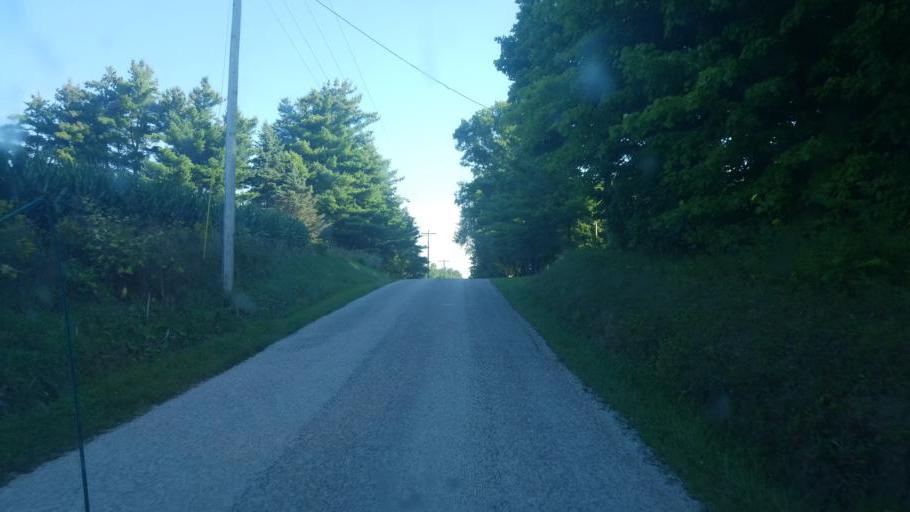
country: US
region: Ohio
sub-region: Ashland County
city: Ashland
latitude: 40.9358
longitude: -82.3398
